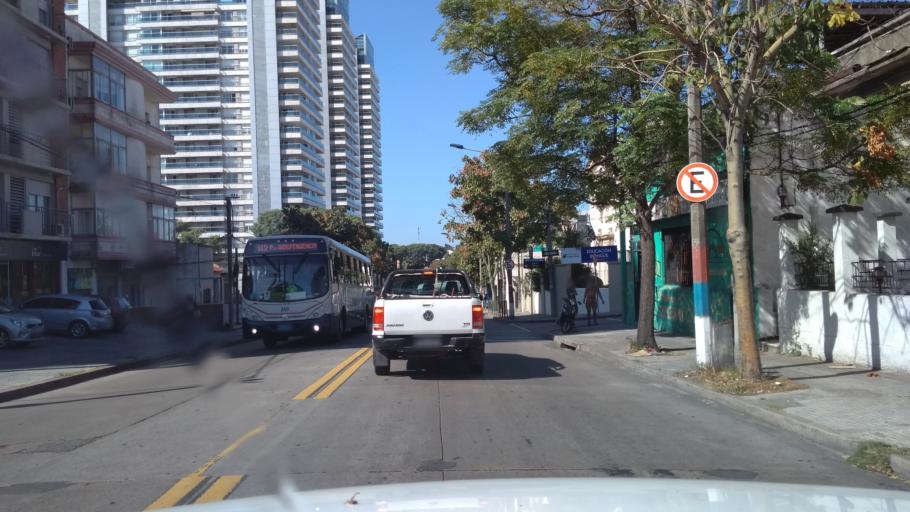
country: UY
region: Montevideo
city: Montevideo
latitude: -34.8964
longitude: -56.1226
